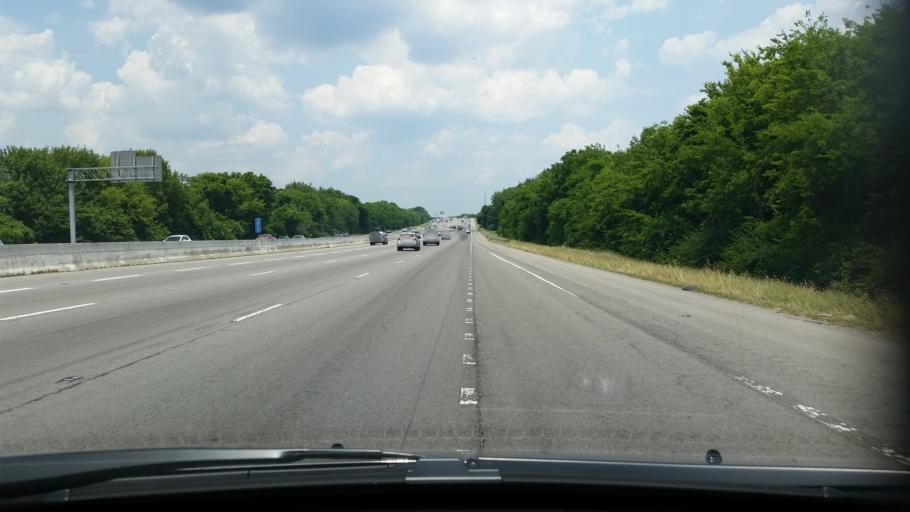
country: US
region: Tennessee
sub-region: Williamson County
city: Brentwood Estates
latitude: 36.0015
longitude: -86.7935
